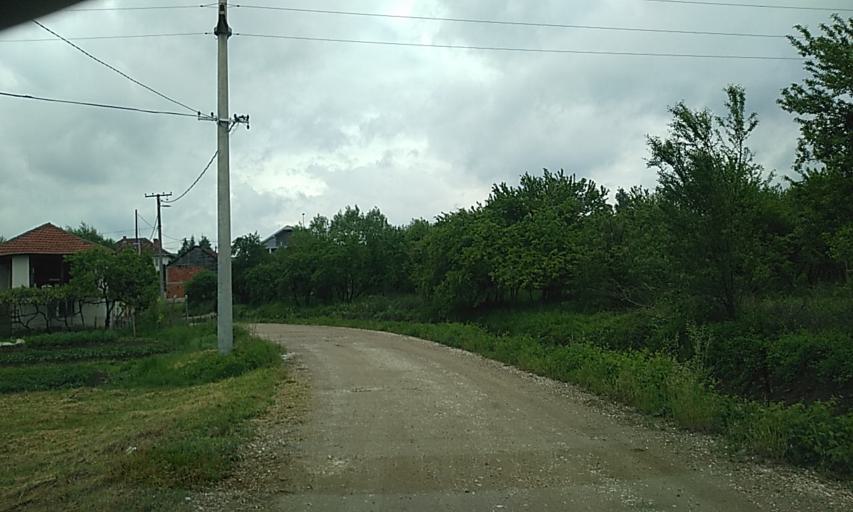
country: RS
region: Central Serbia
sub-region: Pcinjski Okrug
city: Vladicin Han
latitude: 42.7093
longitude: 22.0878
